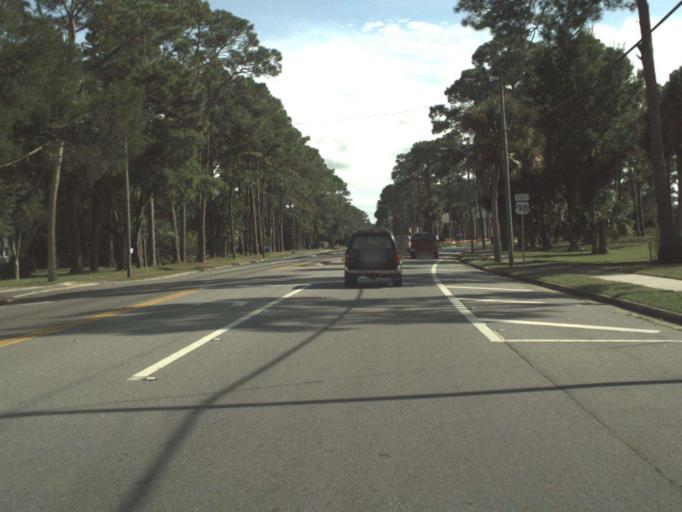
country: US
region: Florida
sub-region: Gulf County
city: Port Saint Joe
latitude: 29.8088
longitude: -85.3022
